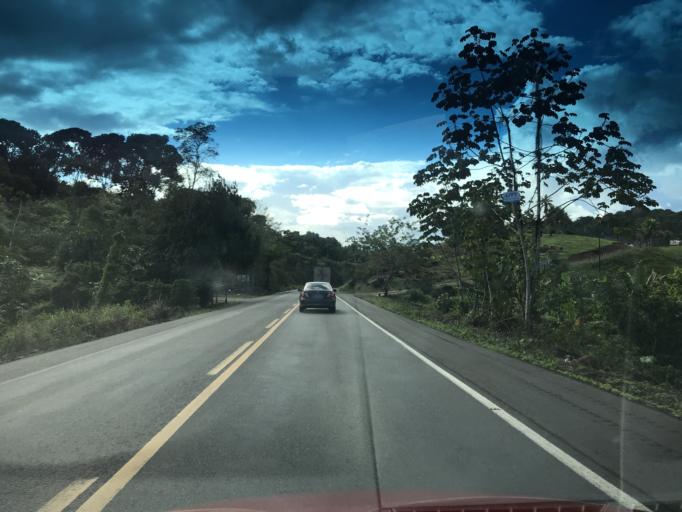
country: BR
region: Bahia
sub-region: Ibirapitanga
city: Ibirapitanga
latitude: -14.1765
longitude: -39.3225
